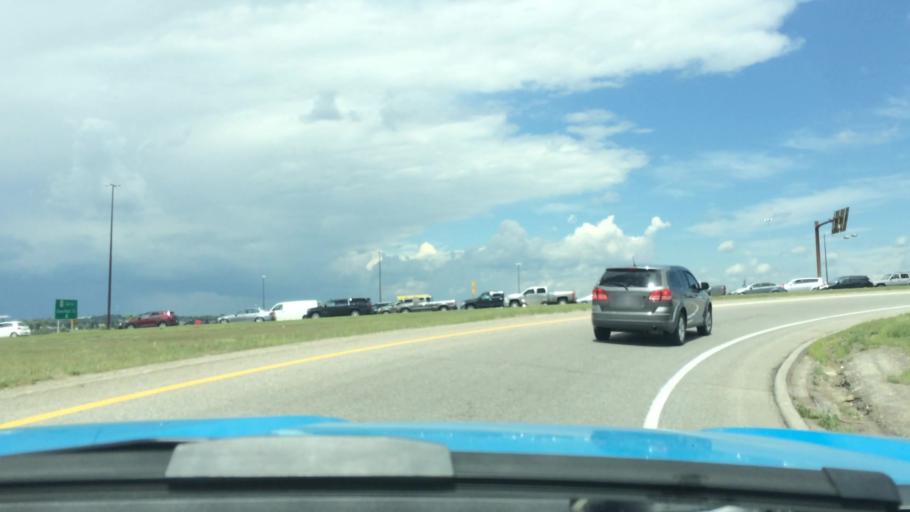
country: CA
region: Alberta
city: Calgary
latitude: 51.0955
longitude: -114.0424
